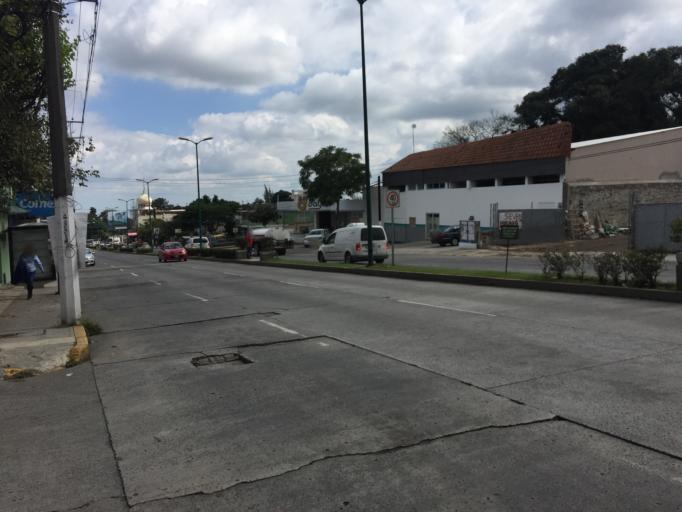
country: MX
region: Veracruz
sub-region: Xalapa
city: Xalapa de Enriquez
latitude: 19.5253
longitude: -96.9015
